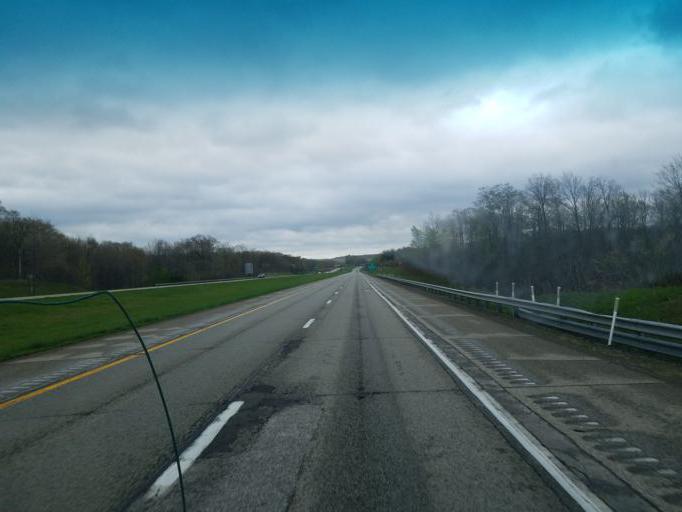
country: US
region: Pennsylvania
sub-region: Erie County
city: North East
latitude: 42.1479
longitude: -79.8505
